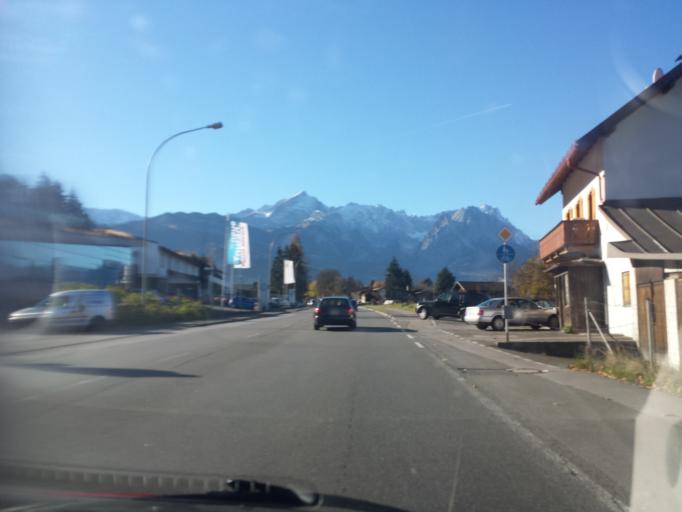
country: DE
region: Bavaria
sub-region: Upper Bavaria
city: Garmisch-Partenkirchen
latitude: 47.5089
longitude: 11.1061
